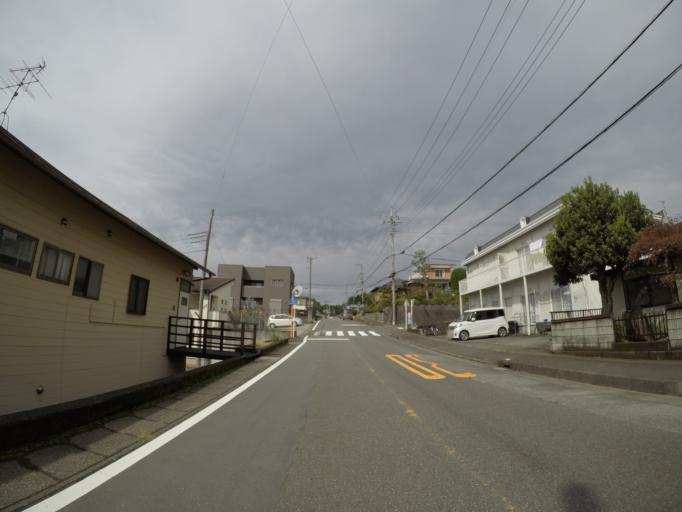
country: JP
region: Shizuoka
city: Fuji
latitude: 35.2228
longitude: 138.6815
